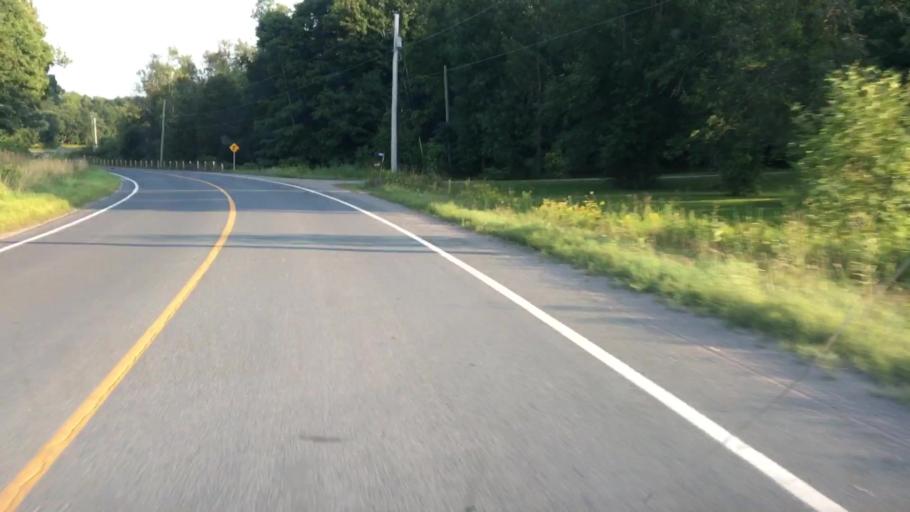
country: CA
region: Ontario
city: Quinte West
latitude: 44.0959
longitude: -77.7350
